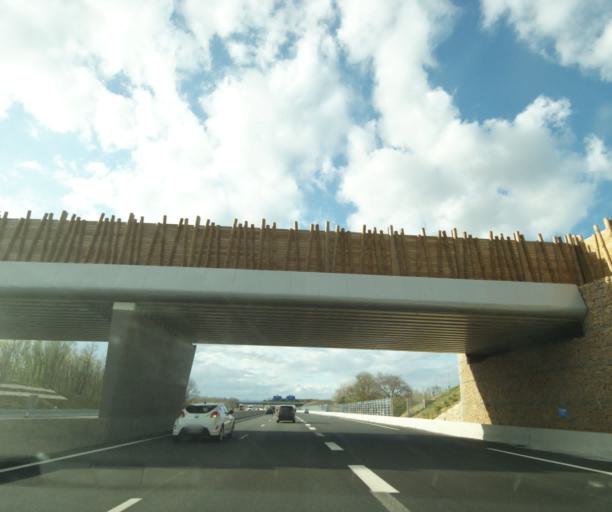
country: FR
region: Rhone-Alpes
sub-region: Departement du Rhone
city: Limonest
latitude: 45.8334
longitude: 4.7598
